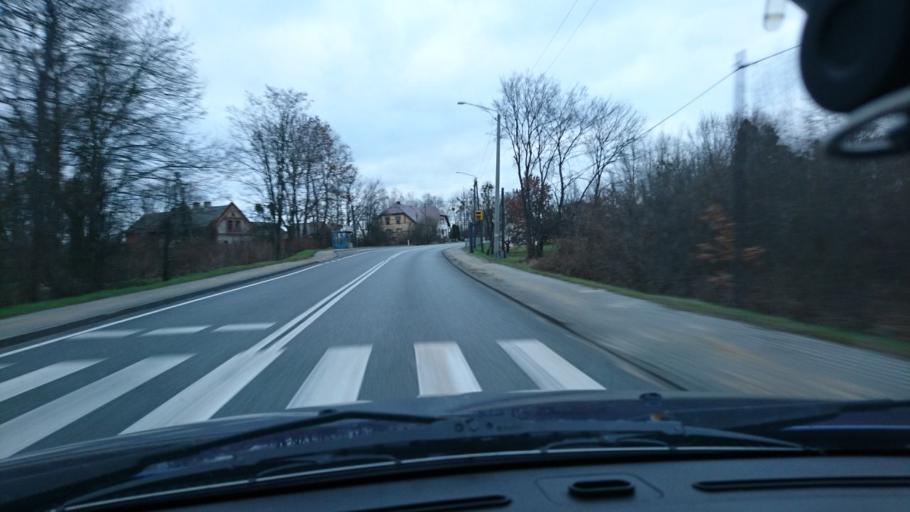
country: PL
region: Opole Voivodeship
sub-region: Powiat kluczborski
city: Byczyna
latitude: 51.0630
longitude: 18.2009
